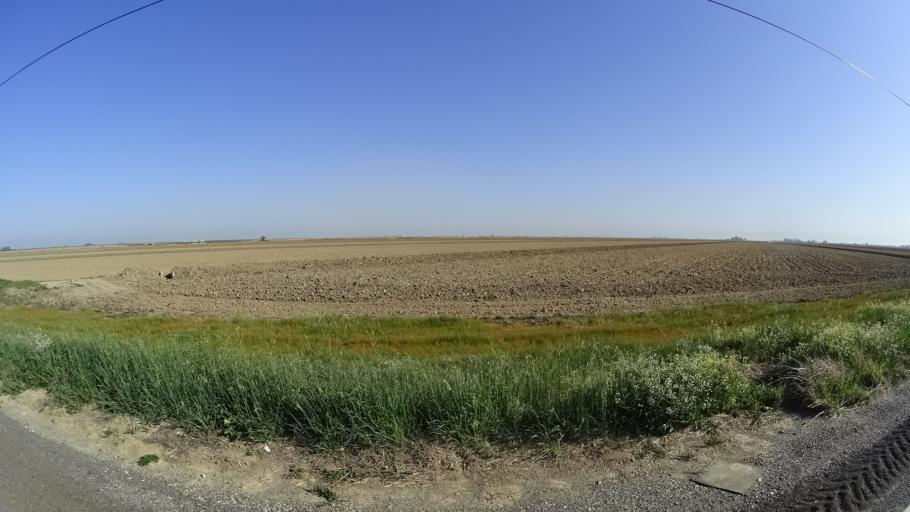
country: US
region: California
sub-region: Glenn County
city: Willows
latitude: 39.5821
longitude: -122.1144
